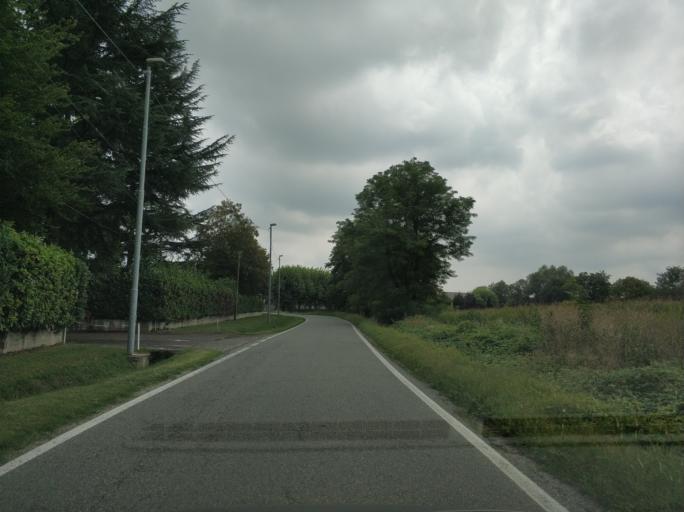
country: IT
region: Piedmont
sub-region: Provincia di Torino
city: Caselle Torinese
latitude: 45.1764
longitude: 7.6290
